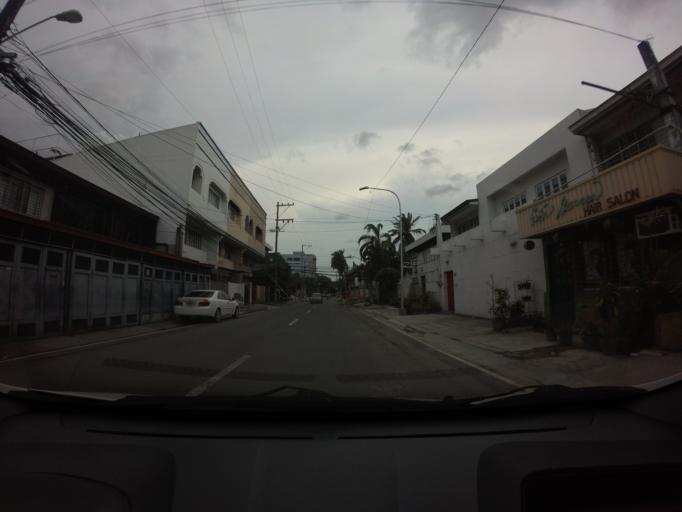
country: PH
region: Calabarzon
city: Del Monte
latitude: 14.6196
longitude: 121.0077
